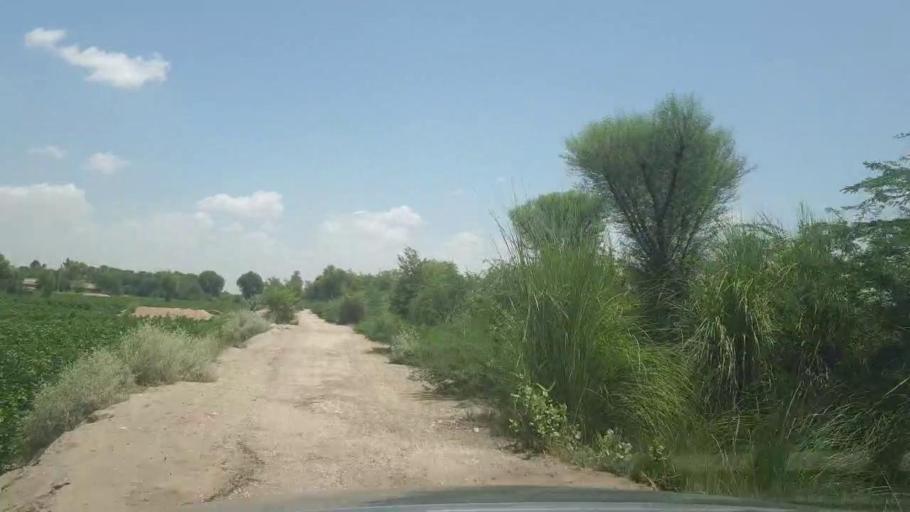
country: PK
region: Sindh
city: Kot Diji
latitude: 27.2631
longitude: 69.0236
